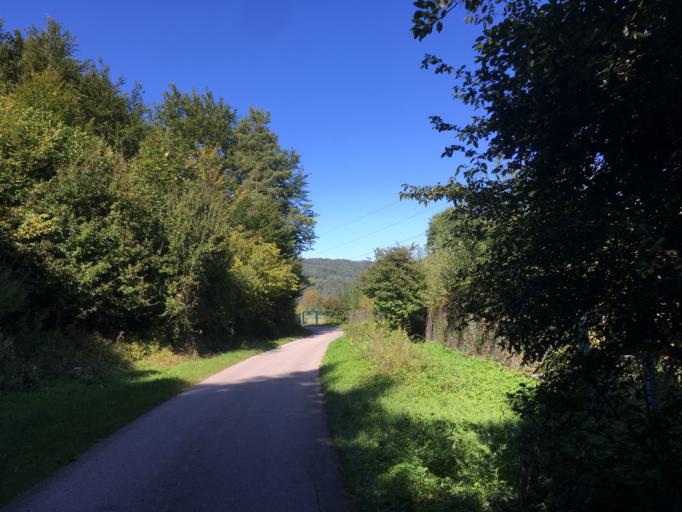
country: SK
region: Trenciansky
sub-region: Okres Povazska Bystrica
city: Povazska Bystrica
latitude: 49.0294
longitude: 18.4348
